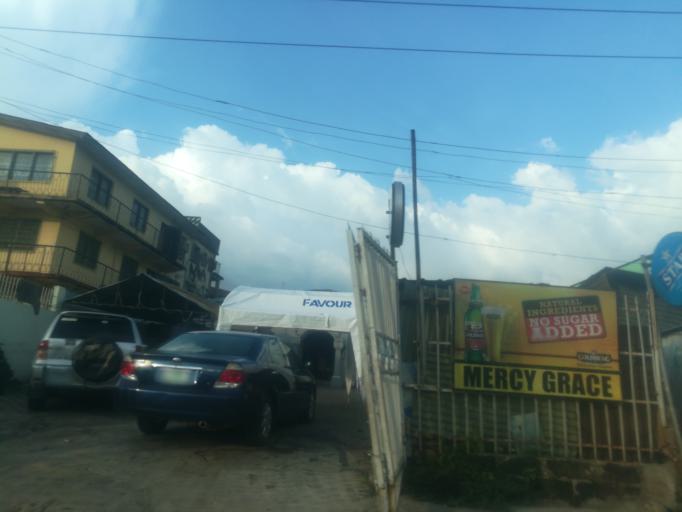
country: NG
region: Oyo
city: Ibadan
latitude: 7.3781
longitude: 3.8550
